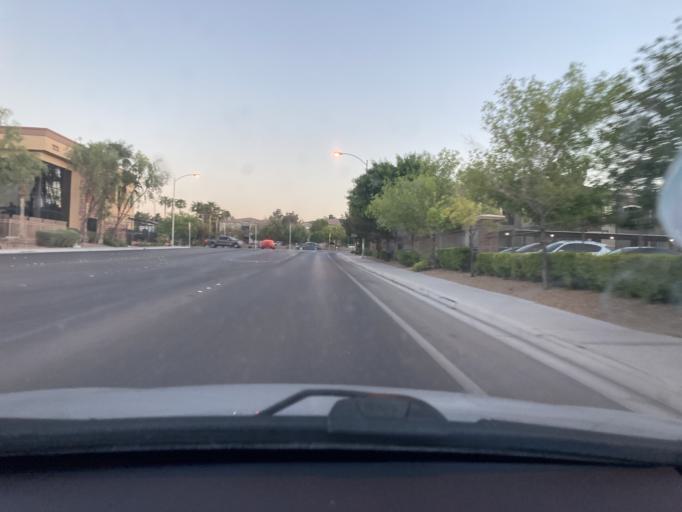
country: US
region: Nevada
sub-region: Clark County
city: Enterprise
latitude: 36.0564
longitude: -115.2882
